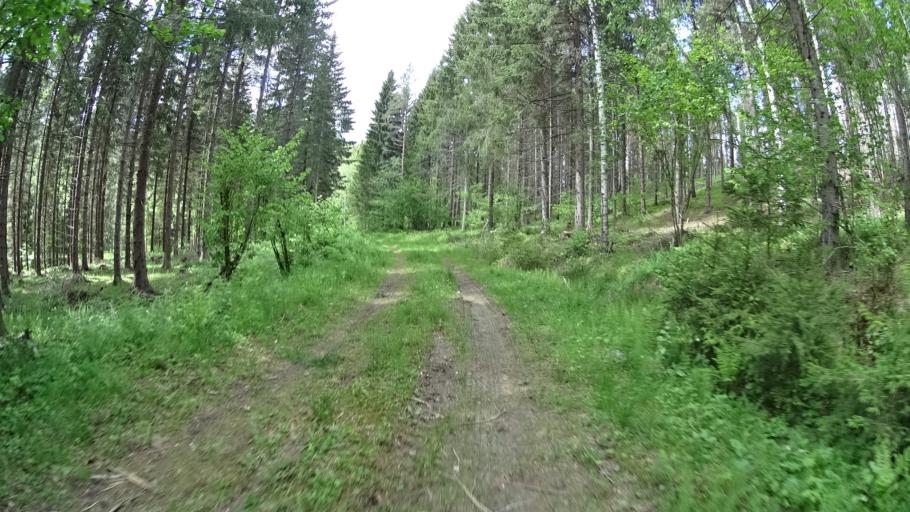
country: FI
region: Uusimaa
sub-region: Raaseporin
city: Pohja
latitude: 60.1641
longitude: 23.6062
